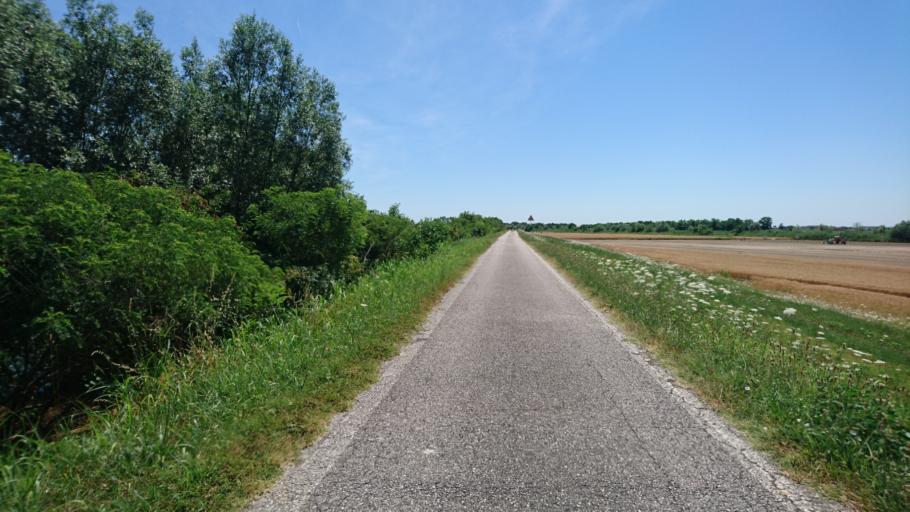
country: IT
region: Veneto
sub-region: Provincia di Venezia
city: Valli
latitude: 45.2184
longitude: 12.1627
